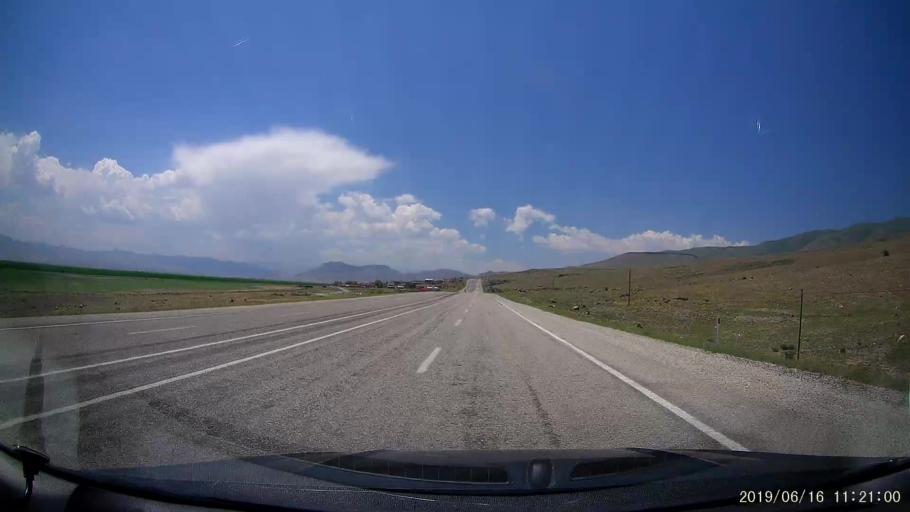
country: TR
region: Agri
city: Dogubayazit
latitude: 39.6976
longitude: 44.0780
